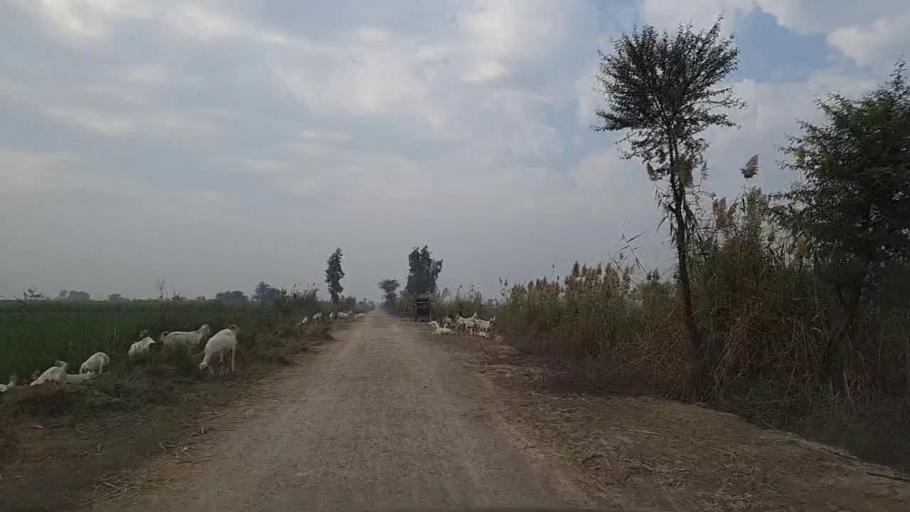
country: PK
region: Sindh
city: Nawabshah
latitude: 26.3609
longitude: 68.3854
